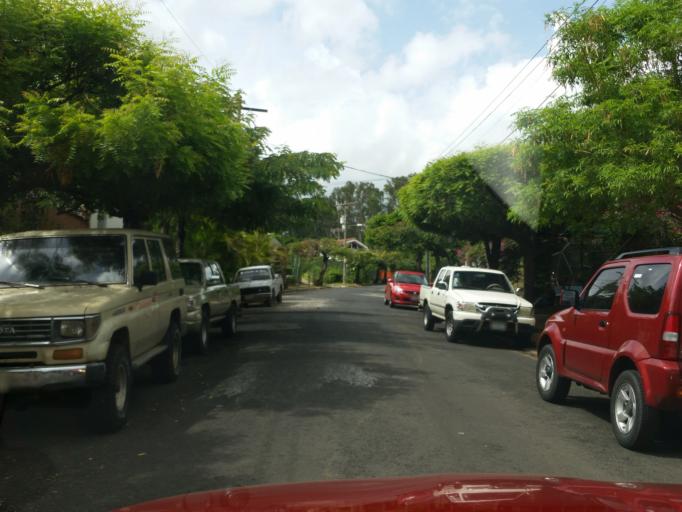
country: NI
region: Managua
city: Managua
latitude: 12.1155
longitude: -86.2776
